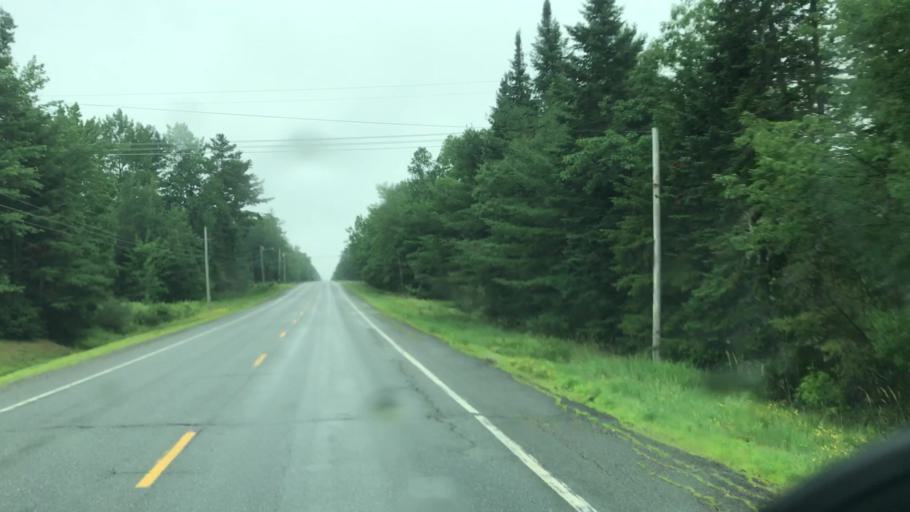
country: US
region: Maine
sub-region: Penobscot County
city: Enfield
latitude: 45.3197
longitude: -68.5998
